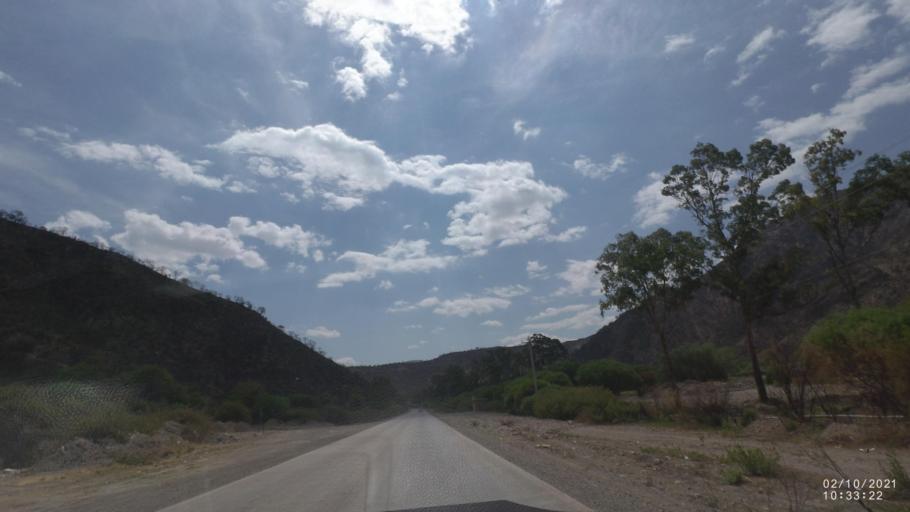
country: BO
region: Cochabamba
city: Capinota
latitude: -17.6815
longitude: -66.2546
